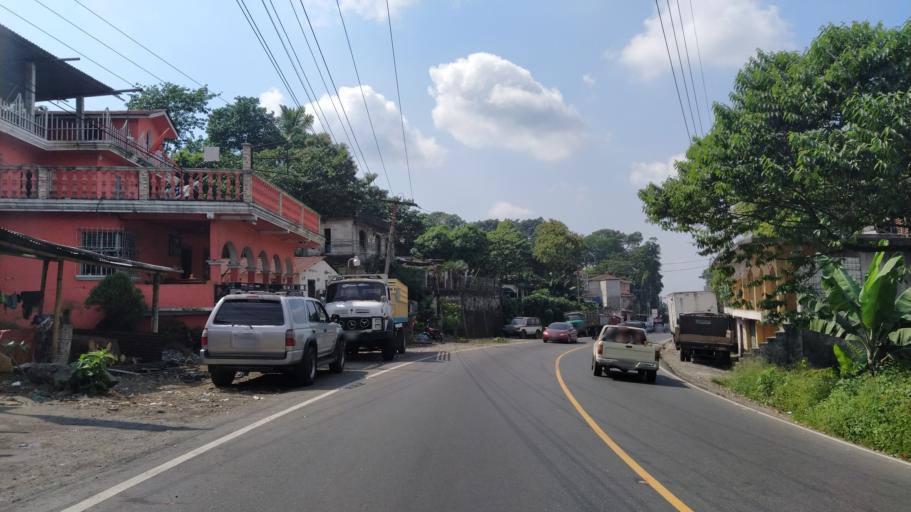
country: GT
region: Quetzaltenango
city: El Palmar
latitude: 14.6348
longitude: -91.5771
